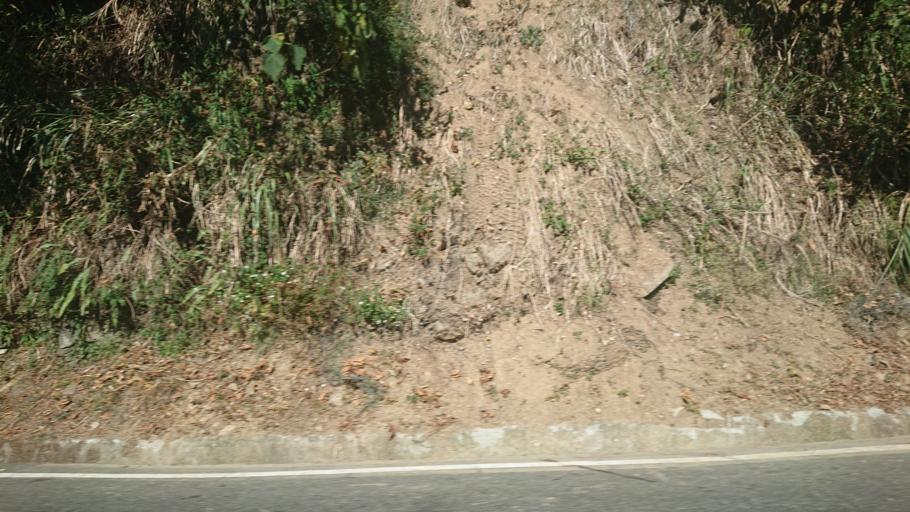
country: TW
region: Taiwan
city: Lugu
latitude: 23.4889
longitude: 120.7798
